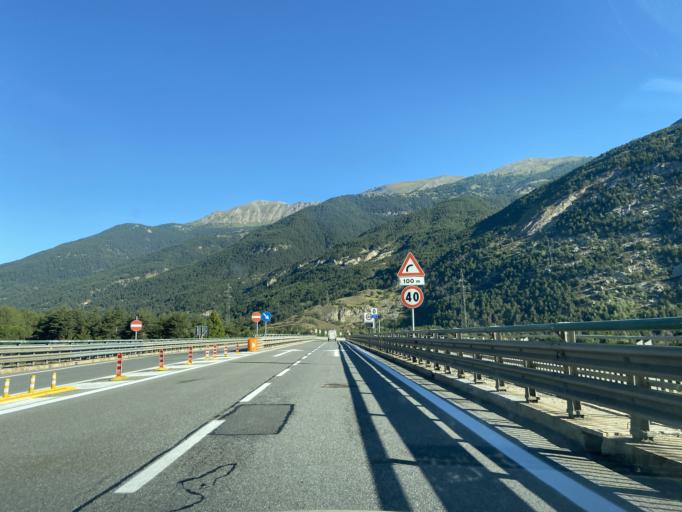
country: IT
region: Piedmont
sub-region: Provincia di Torino
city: Oulx
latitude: 45.0363
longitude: 6.8175
